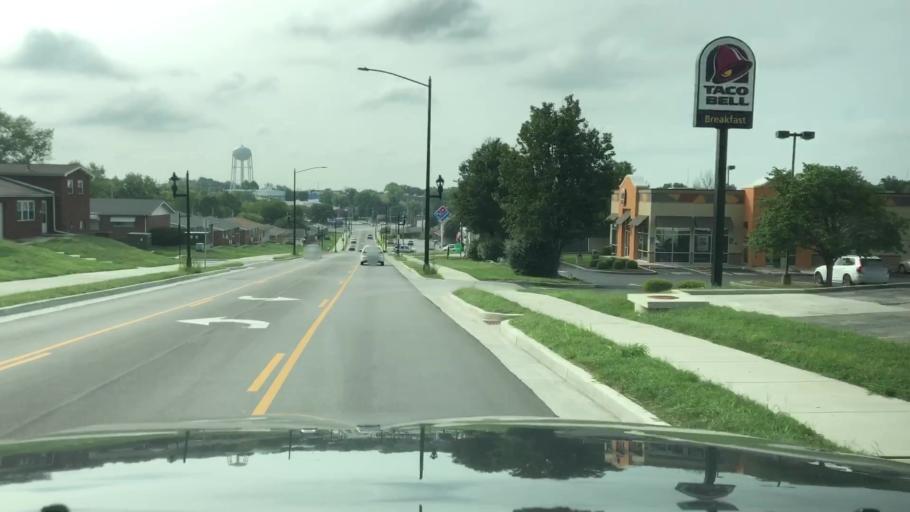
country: US
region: Missouri
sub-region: Saint Charles County
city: Saint Charles
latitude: 38.7882
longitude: -90.5125
